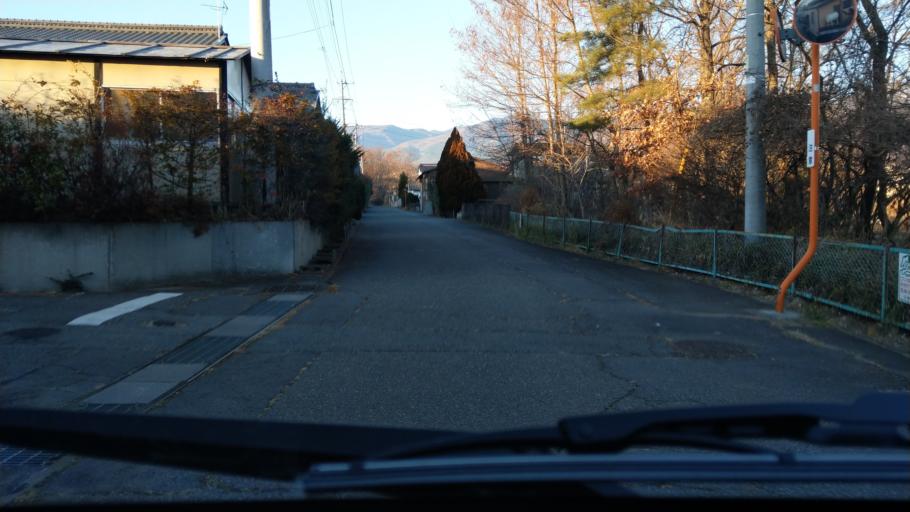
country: JP
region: Nagano
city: Komoro
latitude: 36.3174
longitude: 138.4560
